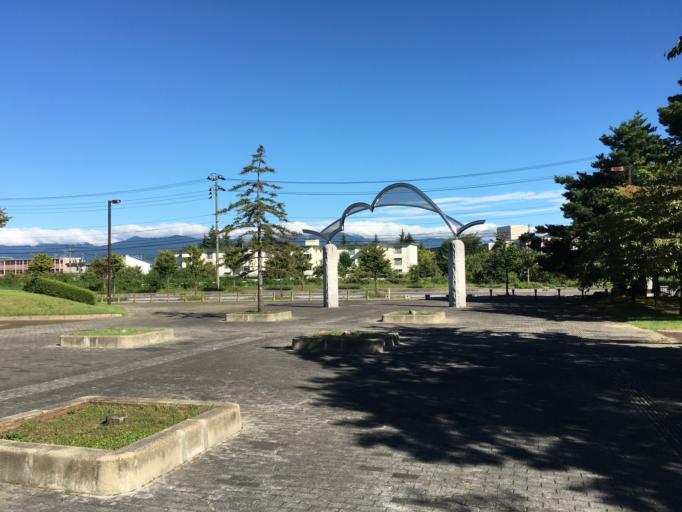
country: JP
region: Yamagata
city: Yonezawa
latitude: 37.9254
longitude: 140.1065
